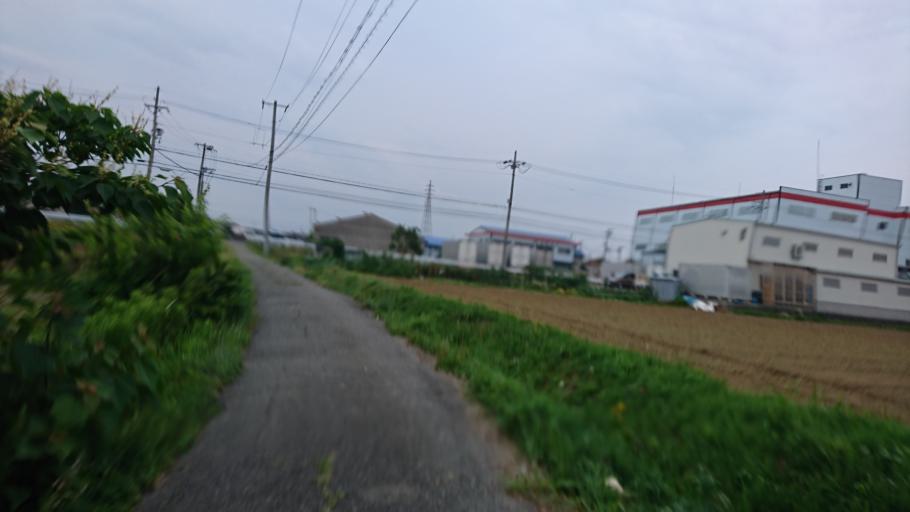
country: JP
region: Hyogo
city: Kakogawacho-honmachi
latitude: 34.7310
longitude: 134.8987
